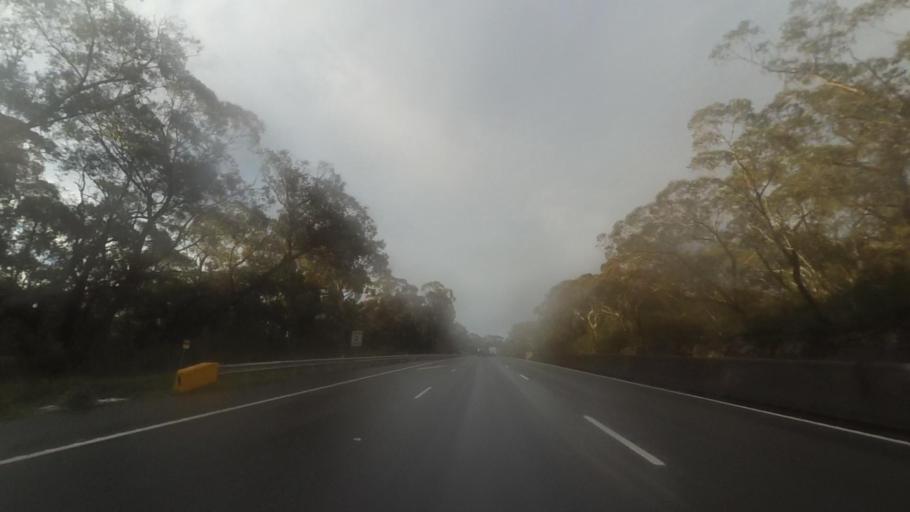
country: AU
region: New South Wales
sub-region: Wollongong
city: Mount Ousley
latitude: -34.3603
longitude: 150.8580
